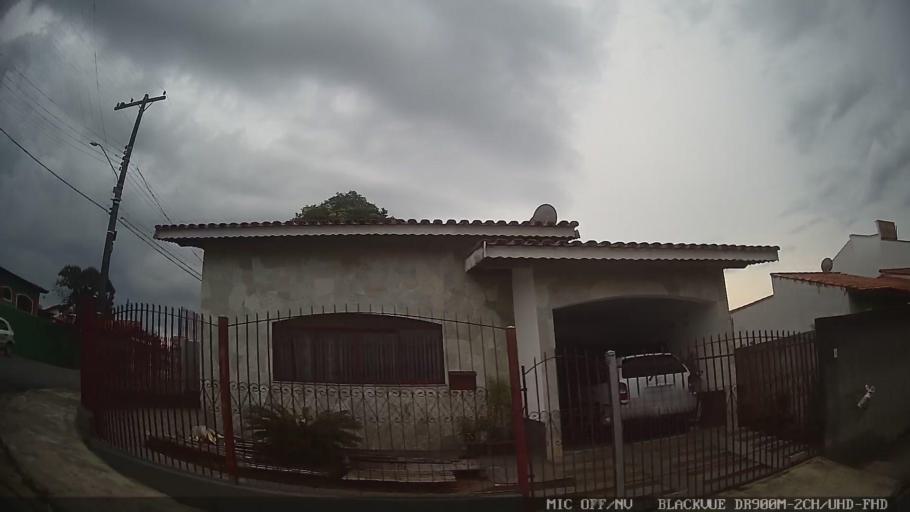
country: BR
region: Sao Paulo
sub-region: Atibaia
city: Atibaia
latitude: -23.1321
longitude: -46.5626
